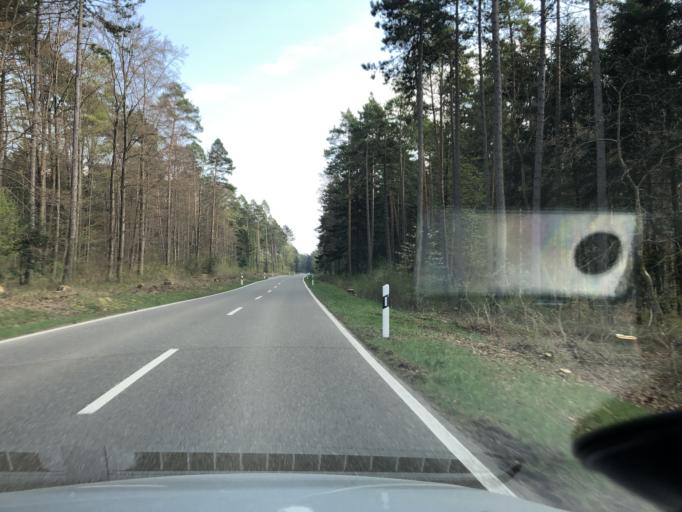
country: DE
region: Baden-Wuerttemberg
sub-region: Karlsruhe Region
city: Simmozheim
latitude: 48.7605
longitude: 8.8344
